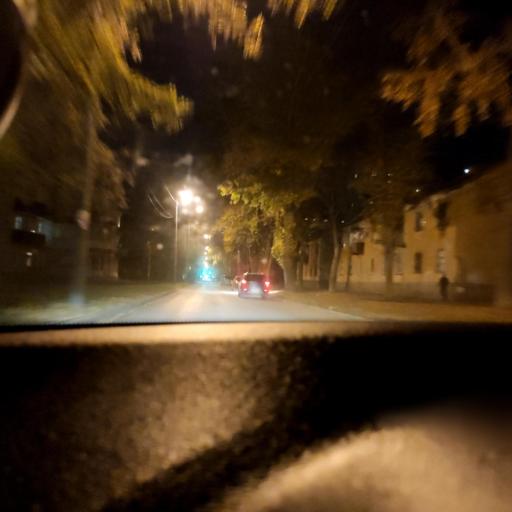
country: RU
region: Samara
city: Samara
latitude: 53.2177
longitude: 50.2499
